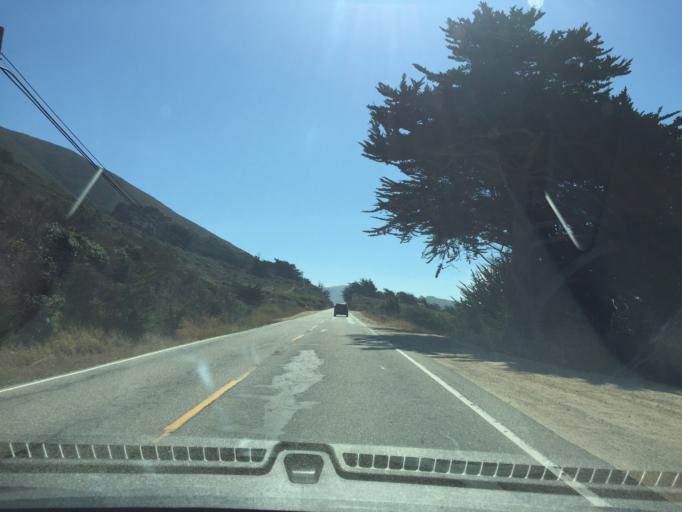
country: US
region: California
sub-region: Monterey County
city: Carmel-by-the-Sea
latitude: 36.3962
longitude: -121.9030
